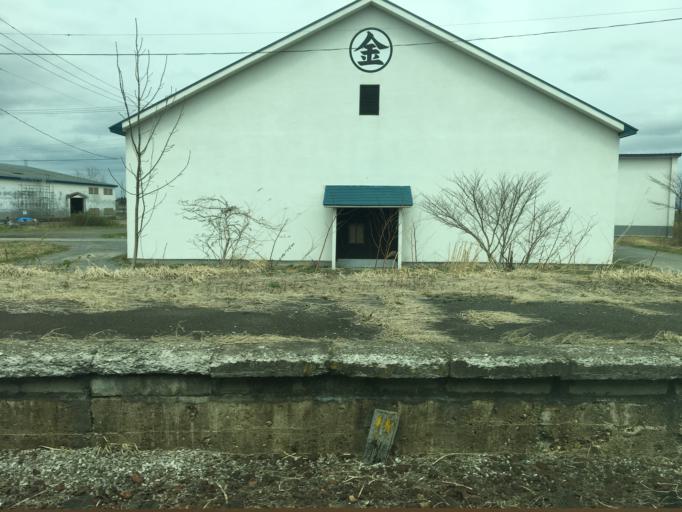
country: JP
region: Aomori
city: Shimokizukuri
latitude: 40.7818
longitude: 140.3385
